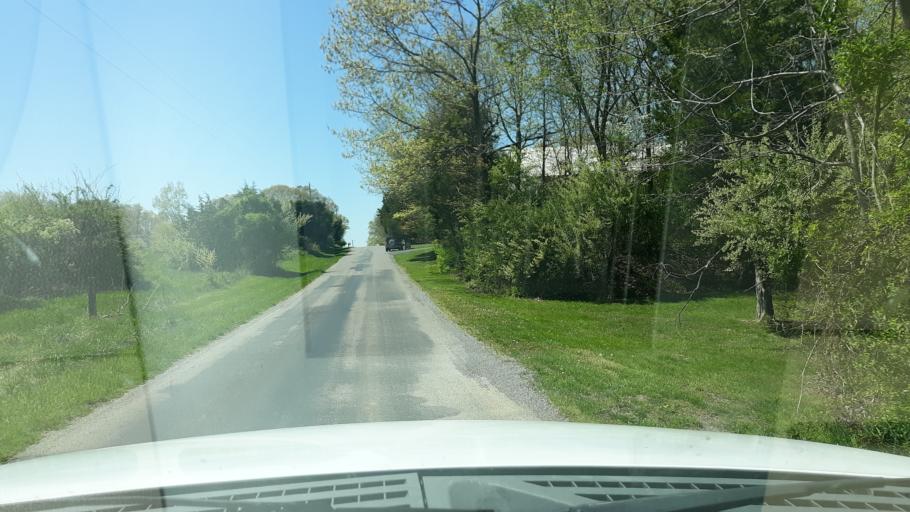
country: US
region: Illinois
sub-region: Saline County
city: Harrisburg
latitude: 37.8596
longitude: -88.6343
